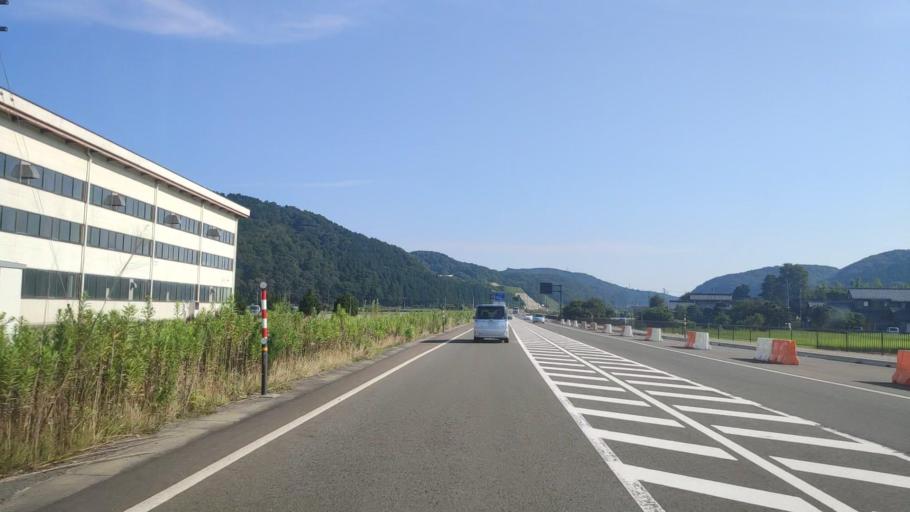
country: JP
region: Fukui
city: Maruoka
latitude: 36.1994
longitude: 136.2673
